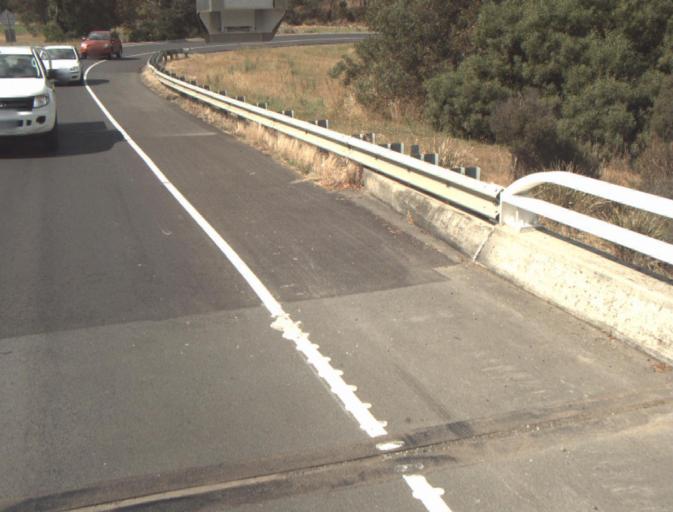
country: AU
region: Tasmania
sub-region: Launceston
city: Summerhill
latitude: -41.4841
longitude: 147.1504
